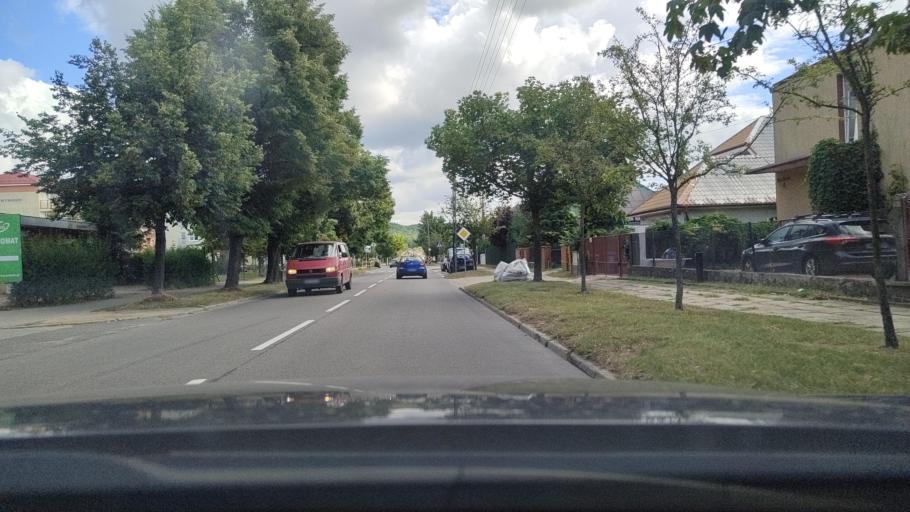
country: PL
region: Pomeranian Voivodeship
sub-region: Powiat wejherowski
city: Wejherowo
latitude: 54.6093
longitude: 18.2252
